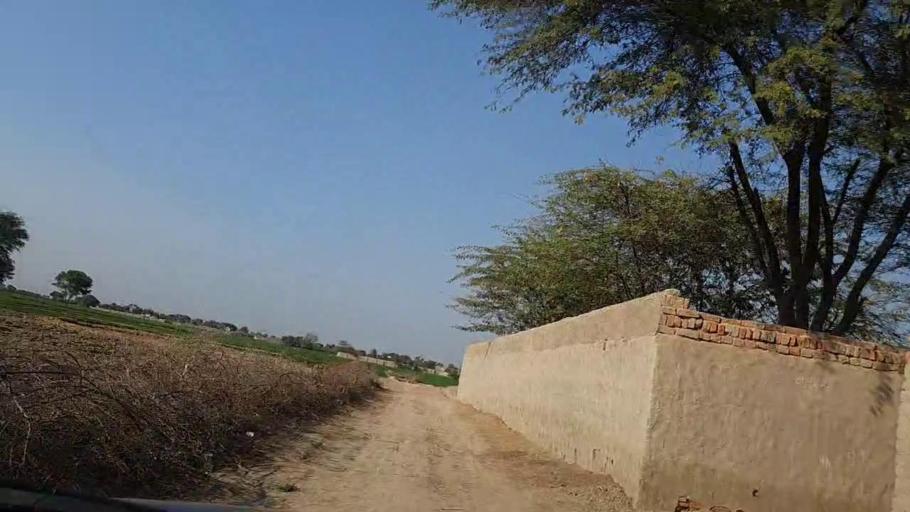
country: PK
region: Sindh
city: Sakrand
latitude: 26.1269
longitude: 68.2379
